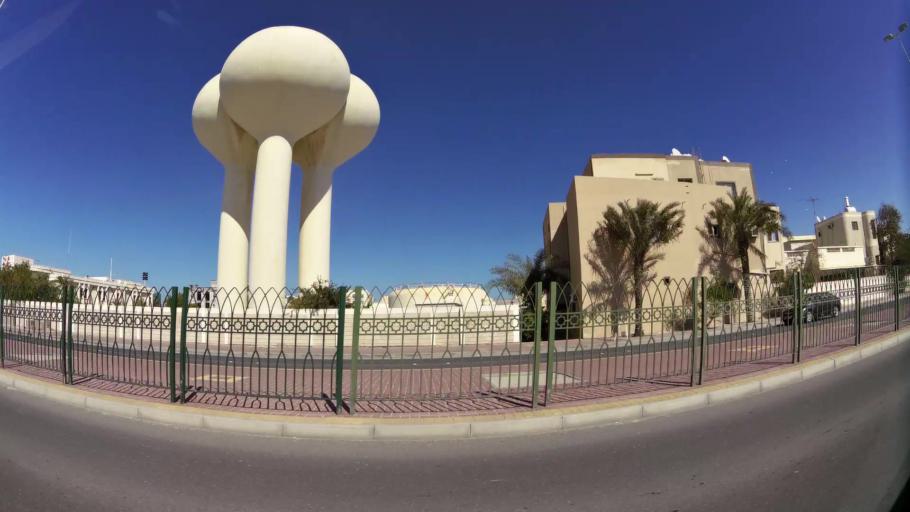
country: BH
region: Muharraq
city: Al Hadd
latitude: 26.2488
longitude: 50.6518
